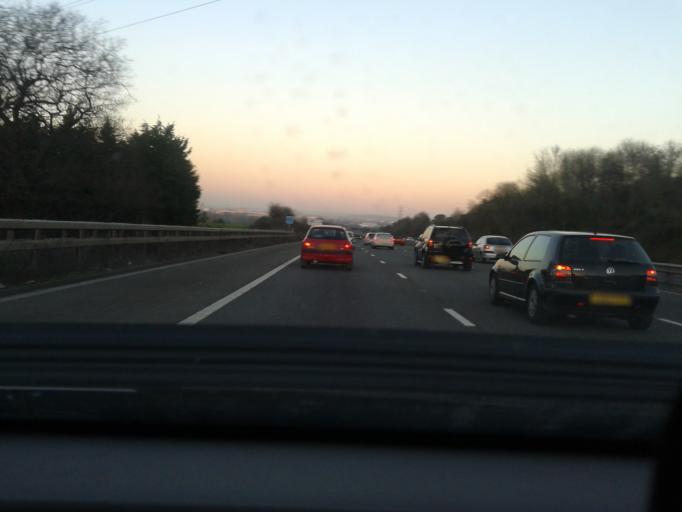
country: GB
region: England
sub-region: North Somerset
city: Portishead
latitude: 51.4642
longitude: -2.7486
